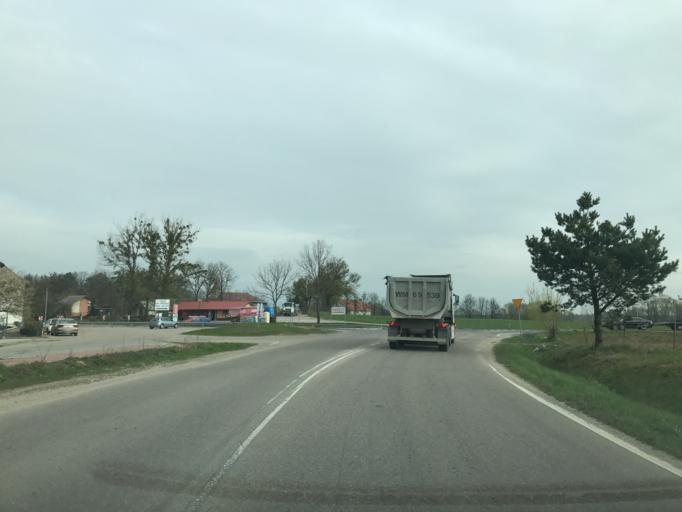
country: PL
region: Warmian-Masurian Voivodeship
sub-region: Powiat ostrodzki
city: Gierzwald
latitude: 53.5838
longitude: 20.0886
